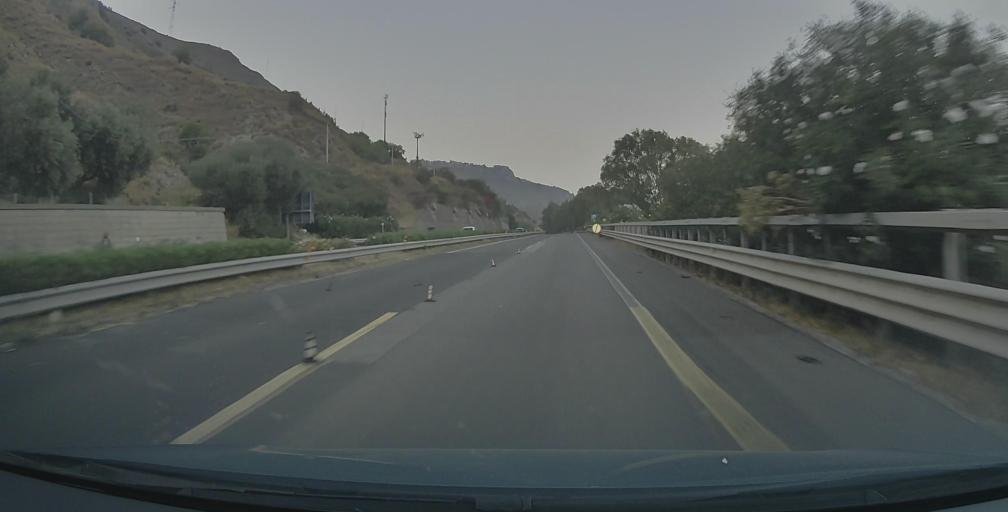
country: IT
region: Sicily
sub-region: Messina
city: Letojanni
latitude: 37.8937
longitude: 15.3211
